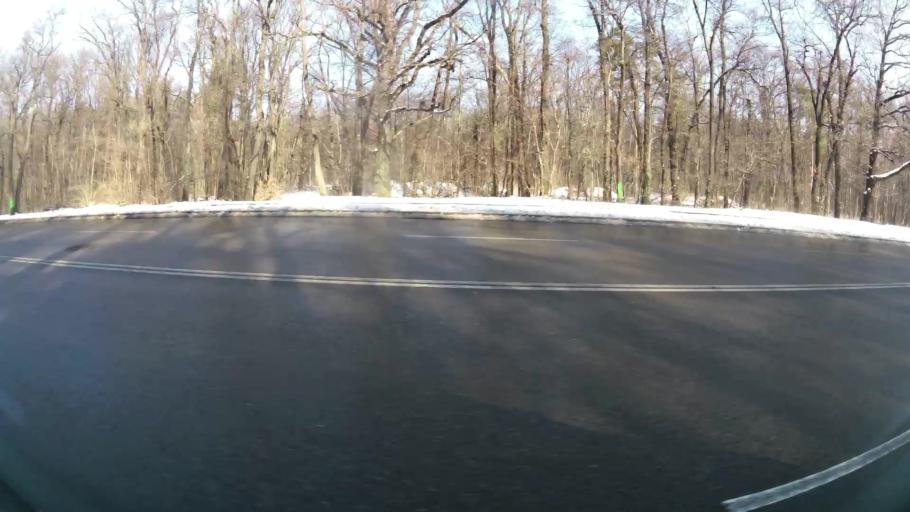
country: BG
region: Sofia-Capital
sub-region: Stolichna Obshtina
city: Sofia
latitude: 42.6709
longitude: 23.3376
